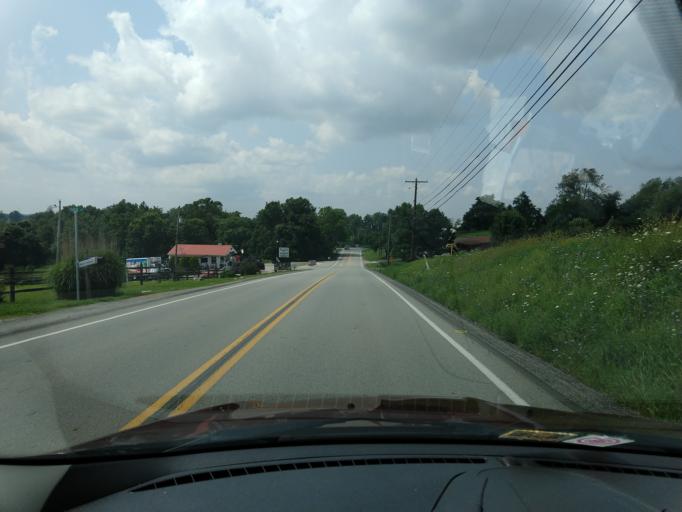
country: US
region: Pennsylvania
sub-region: Washington County
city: Ellsworth
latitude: 40.1857
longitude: -80.0529
